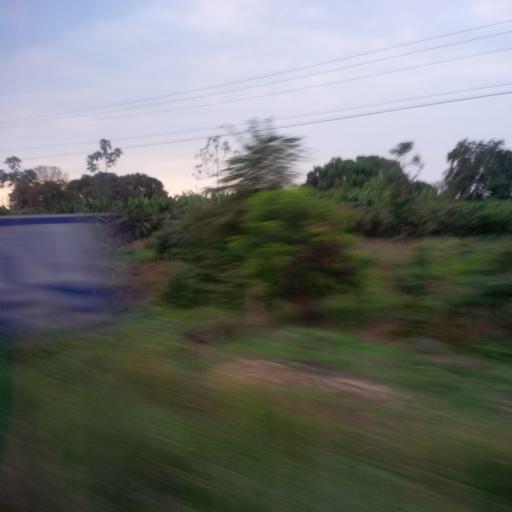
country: EC
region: Guayas
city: Coronel Marcelino Mariduena
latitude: -2.3322
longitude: -79.4304
